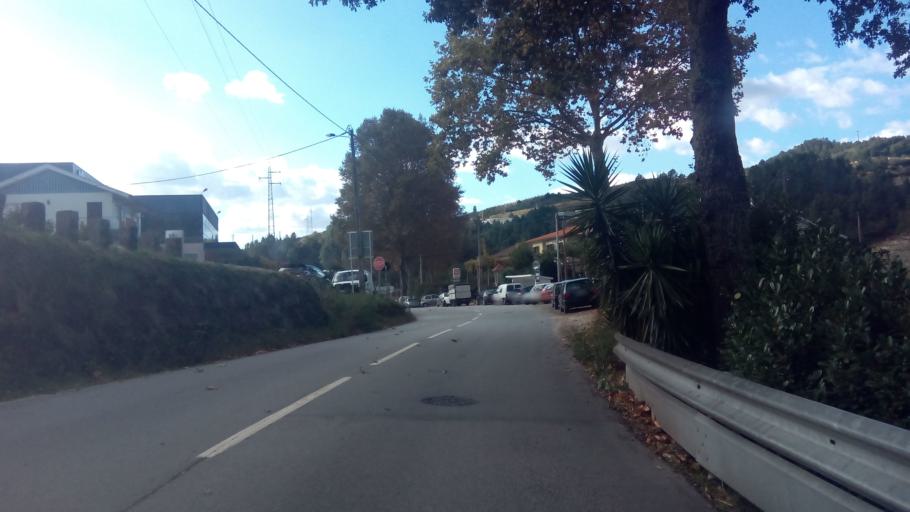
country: PT
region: Porto
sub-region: Amarante
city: Amarante
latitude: 41.2554
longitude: -8.0288
